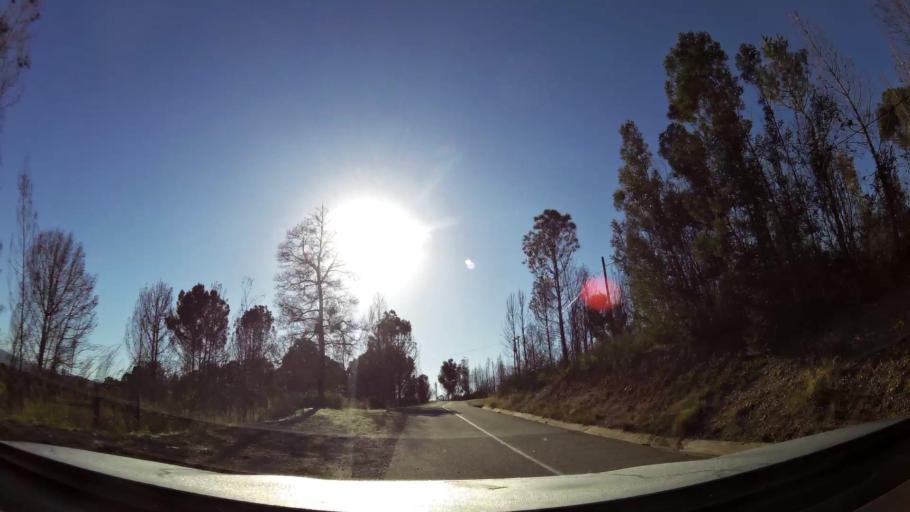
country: ZA
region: Western Cape
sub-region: Eden District Municipality
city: Knysna
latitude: -34.0237
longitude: 23.0078
